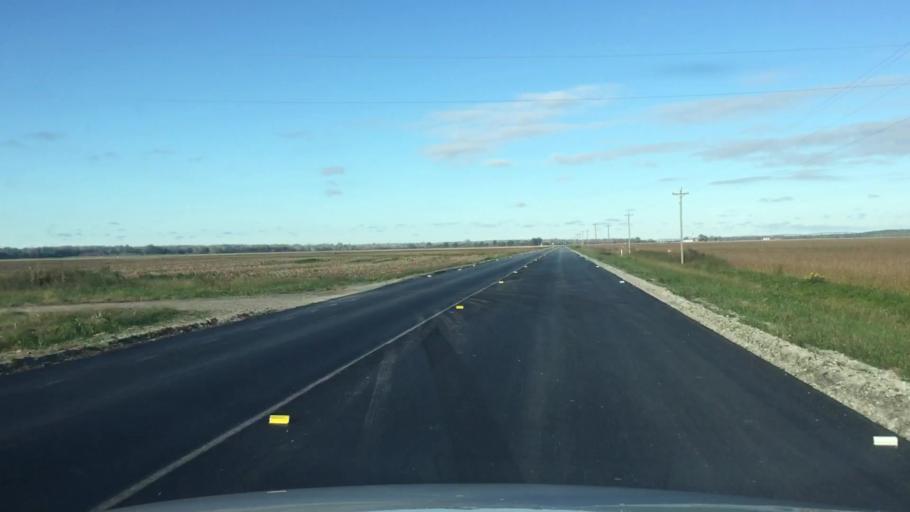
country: US
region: Missouri
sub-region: Howard County
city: New Franklin
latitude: 38.9918
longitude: -92.6319
